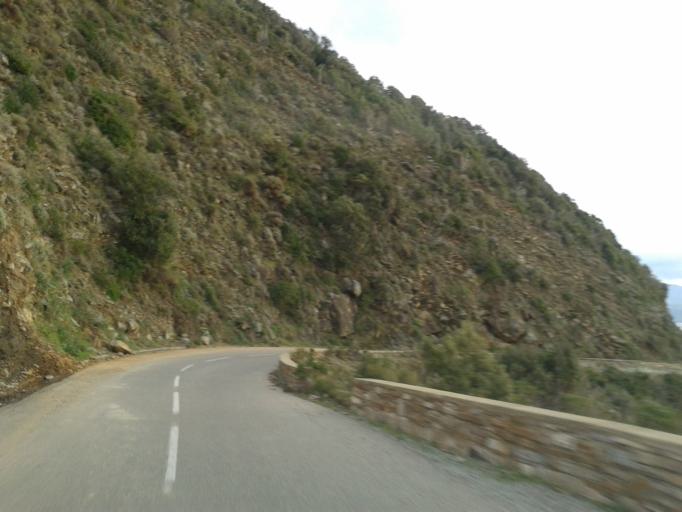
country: FR
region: Corsica
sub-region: Departement de la Haute-Corse
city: Santa-Maria-di-Lota
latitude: 42.7677
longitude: 9.3409
